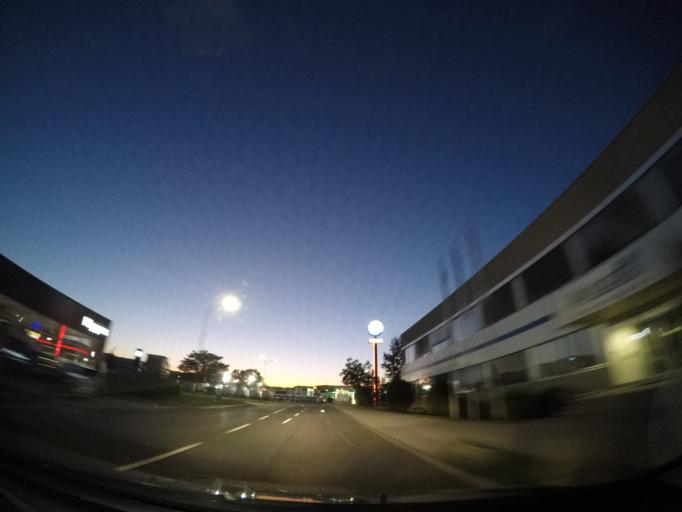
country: AT
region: Lower Austria
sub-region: Politischer Bezirk Modling
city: Wiener Neudorf
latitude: 48.0769
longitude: 16.3257
